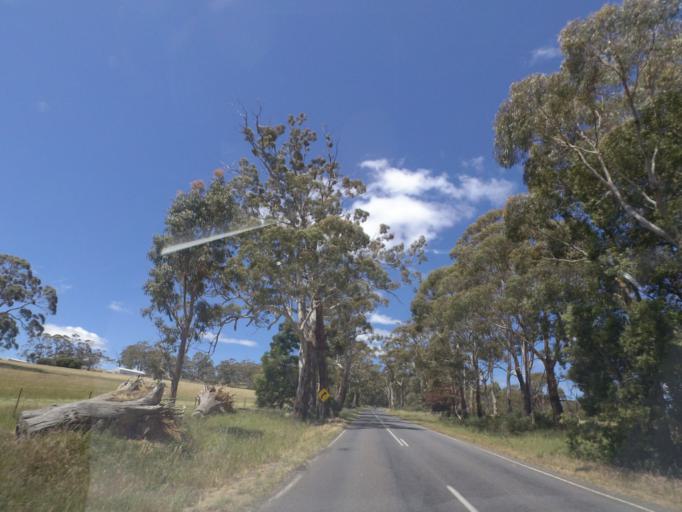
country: AU
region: Victoria
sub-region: Mount Alexander
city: Castlemaine
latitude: -37.2908
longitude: 144.2608
